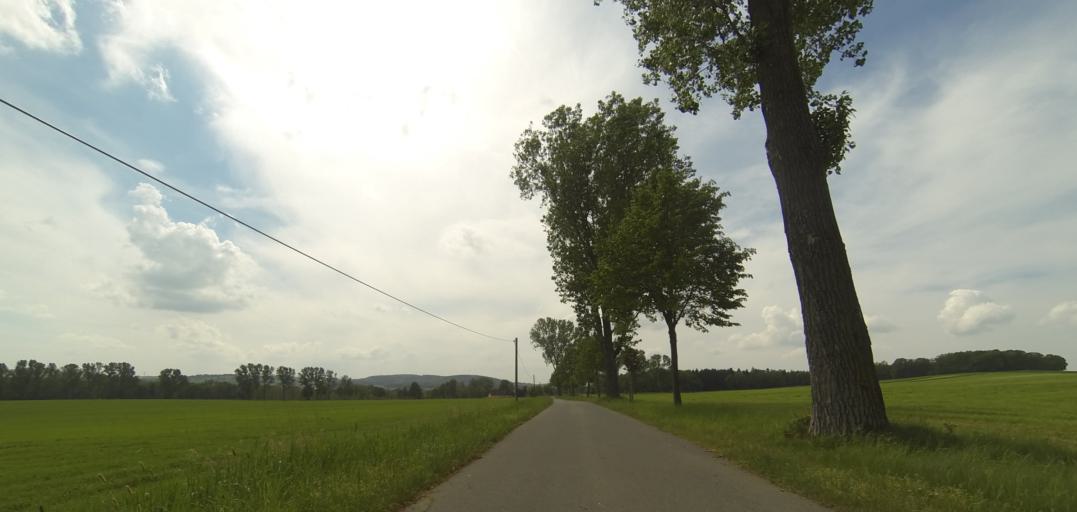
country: DE
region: Saxony
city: Frankenthal
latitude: 51.1117
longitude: 14.1343
